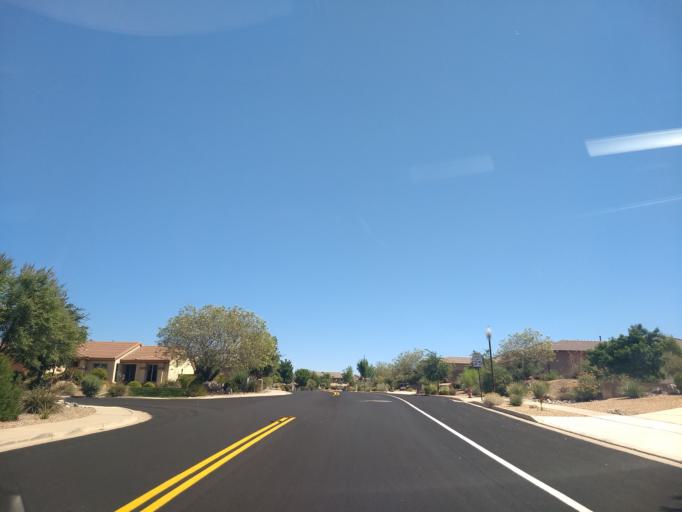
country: US
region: Utah
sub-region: Washington County
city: Washington
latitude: 37.1407
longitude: -113.4668
